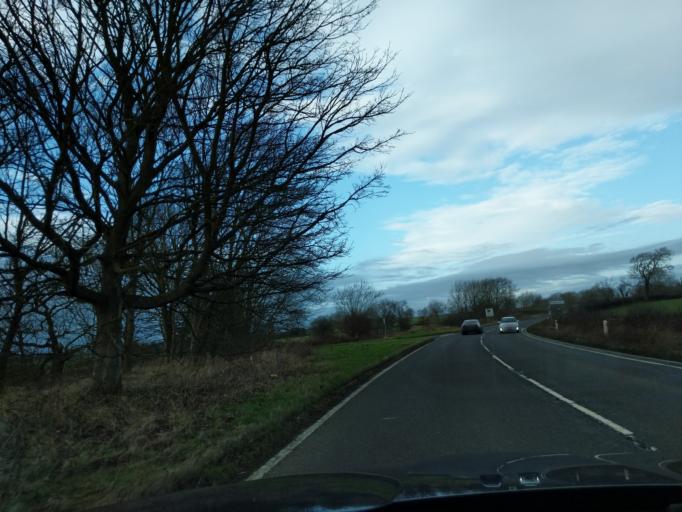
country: GB
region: England
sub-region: Northumberland
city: Meldon
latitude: 55.0789
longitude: -1.8038
